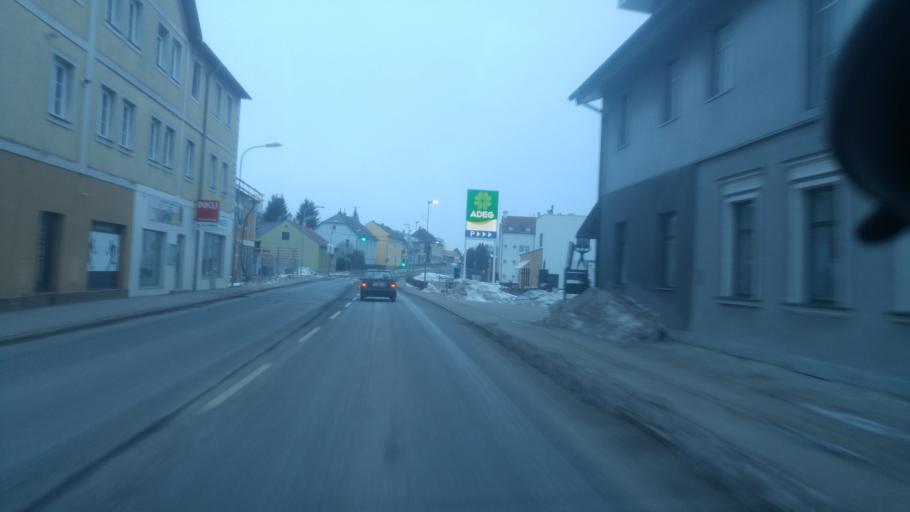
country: AT
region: Lower Austria
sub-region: Politischer Bezirk Lilienfeld
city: Hainfeld
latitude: 48.0366
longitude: 15.7695
